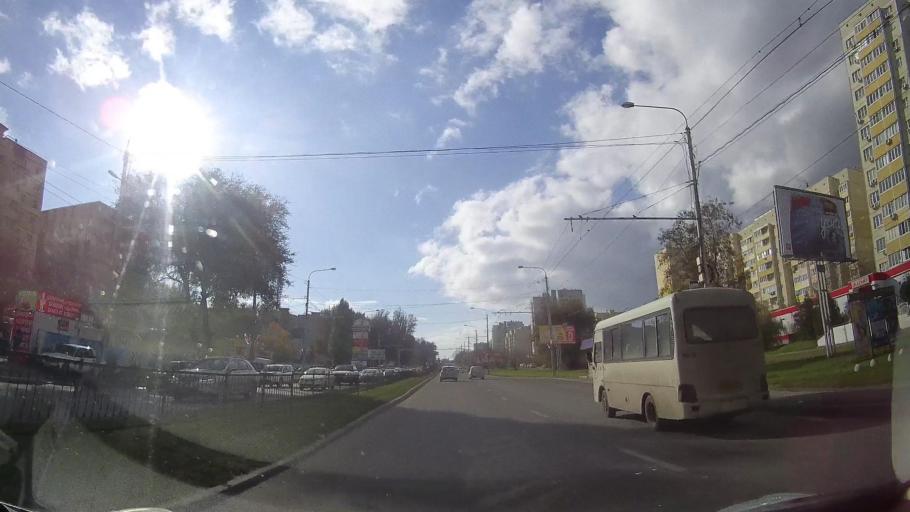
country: RU
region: Rostov
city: Severnyy
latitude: 47.2604
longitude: 39.6516
